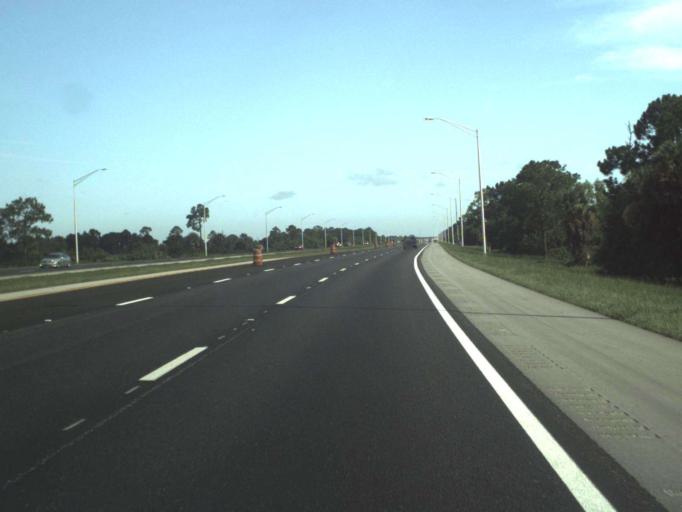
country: US
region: Florida
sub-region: Indian River County
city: West Vero Corridor
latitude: 27.5721
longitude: -80.4917
